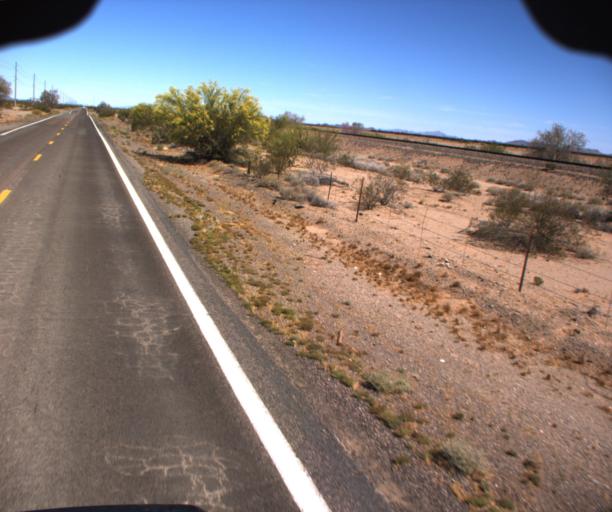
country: US
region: Arizona
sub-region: La Paz County
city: Salome
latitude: 33.8113
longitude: -113.8491
